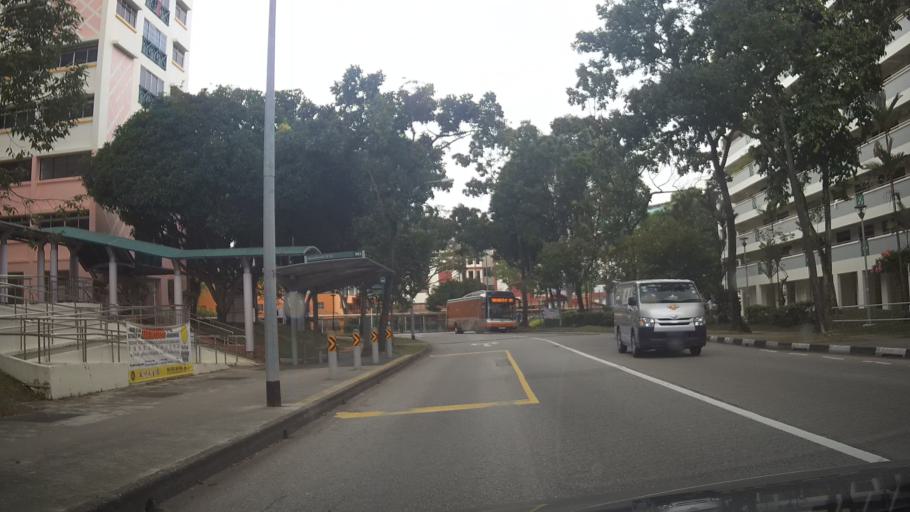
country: MY
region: Johor
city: Johor Bahru
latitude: 1.4422
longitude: 103.7900
